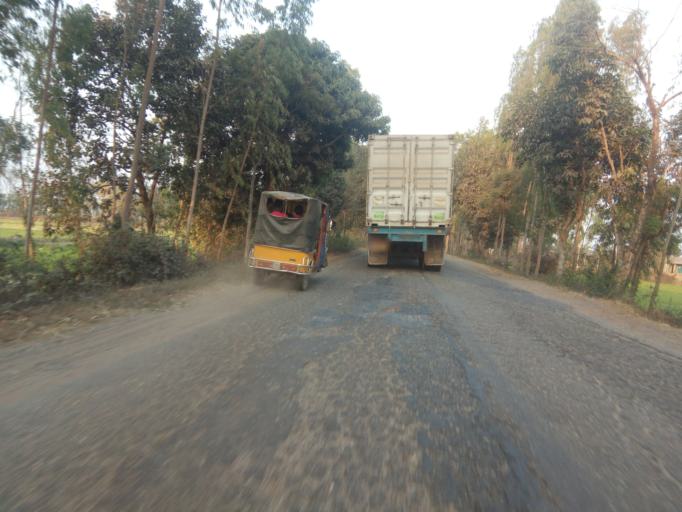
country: BD
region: Rajshahi
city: Bogra
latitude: 24.5640
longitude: 89.2066
